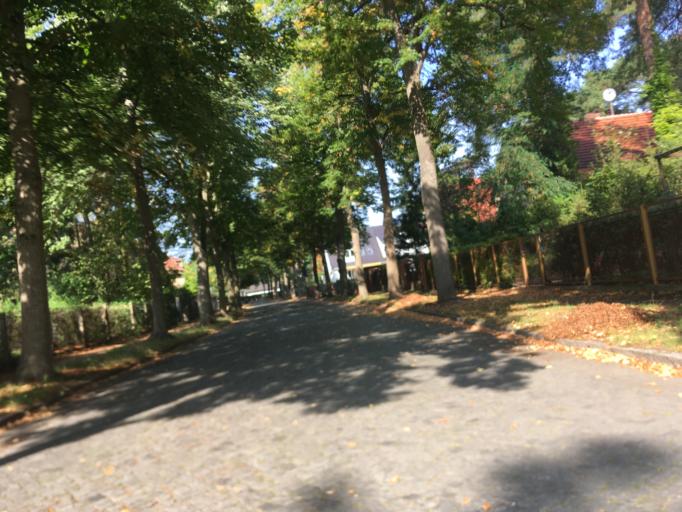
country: DE
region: Brandenburg
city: Zeuthen
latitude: 52.3674
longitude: 13.6309
